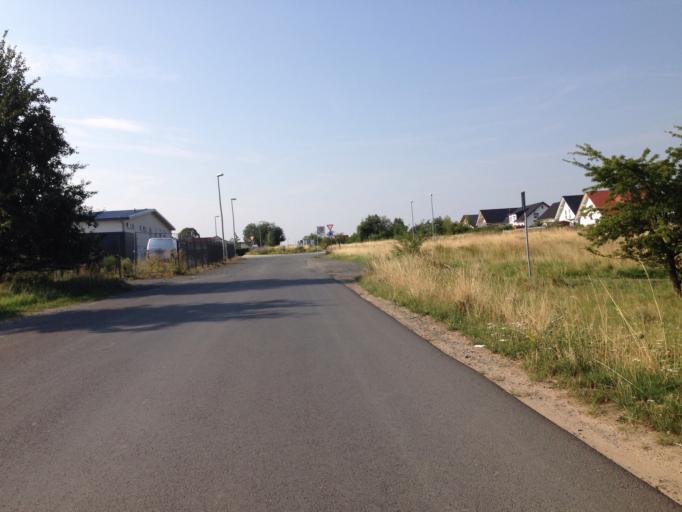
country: DE
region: Hesse
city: Lollar
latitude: 50.6163
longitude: 8.7031
